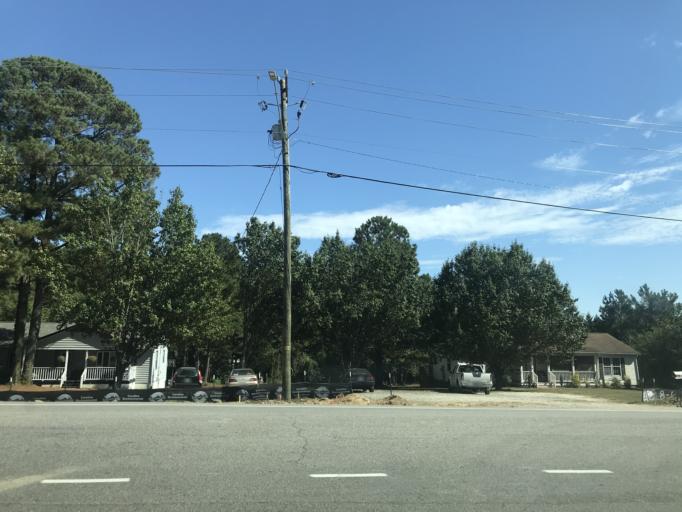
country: US
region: North Carolina
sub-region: Wake County
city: Knightdale
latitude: 35.8603
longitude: -78.5668
